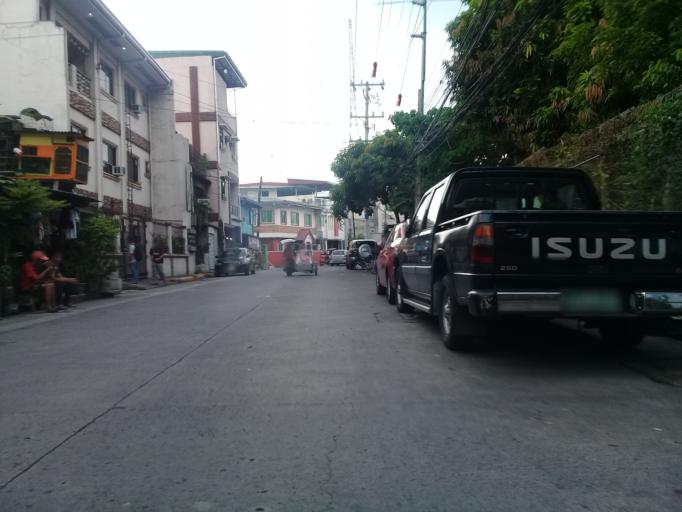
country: PH
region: Metro Manila
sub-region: Mandaluyong
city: Mandaluyong City
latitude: 14.5773
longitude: 121.0168
